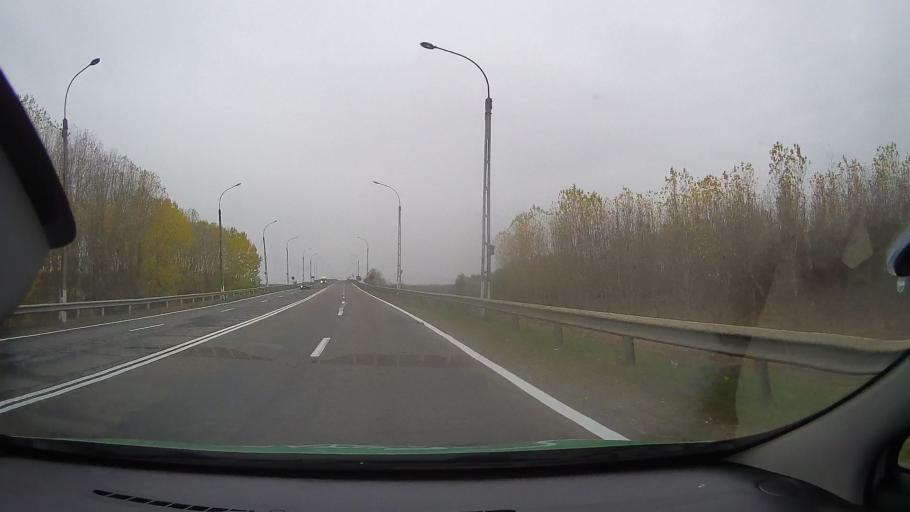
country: RO
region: Ialomita
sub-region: Comuna Giurgeni
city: Giurgeni
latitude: 44.7523
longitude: 27.8888
